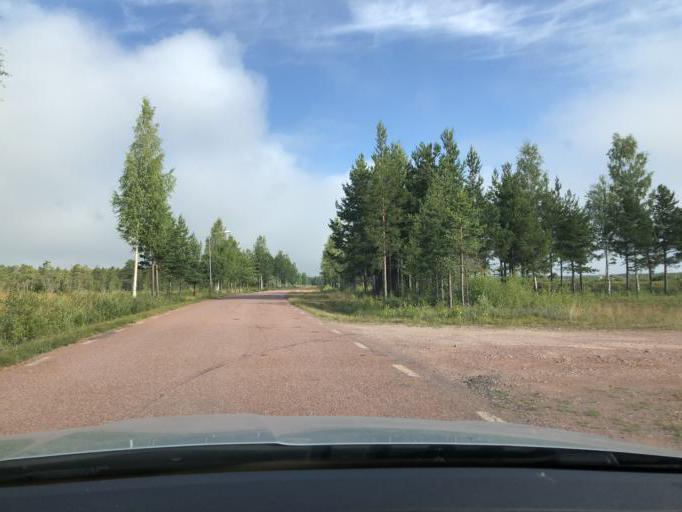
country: SE
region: Dalarna
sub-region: Mora Kommun
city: Mora
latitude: 60.9599
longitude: 14.5023
